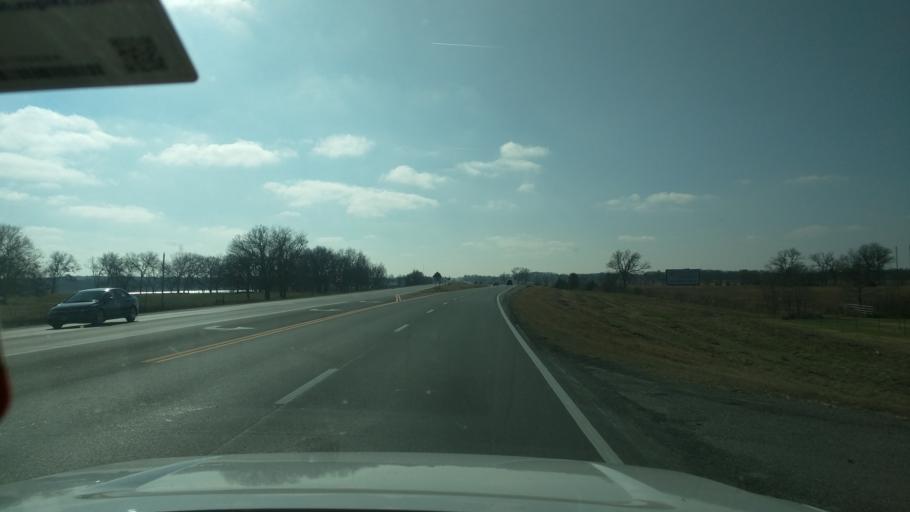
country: US
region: Oklahoma
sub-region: Washington County
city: Bartlesville
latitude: 36.6679
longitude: -95.9353
